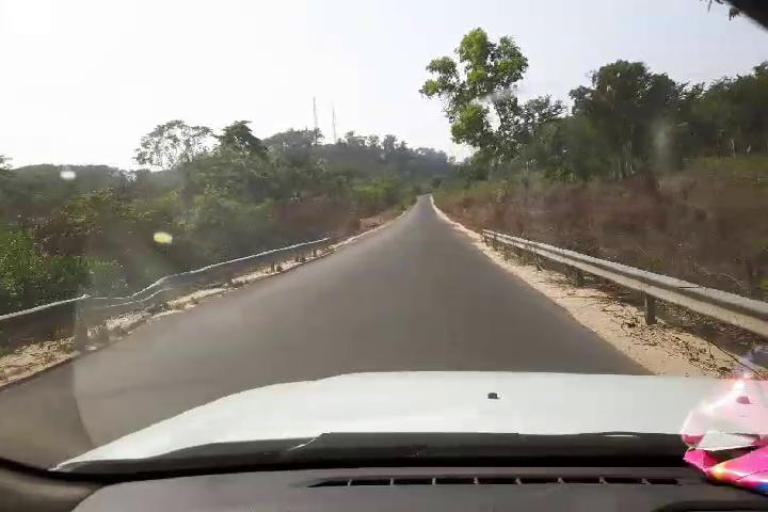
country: SL
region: Western Area
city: Waterloo
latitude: 8.2605
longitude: -13.1606
